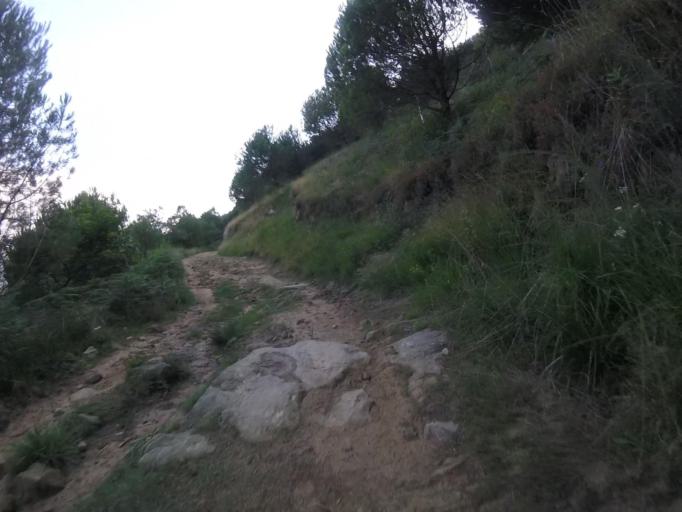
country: ES
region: Basque Country
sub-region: Provincia de Guipuzcoa
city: Fuenterrabia
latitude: 43.3512
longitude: -1.8400
